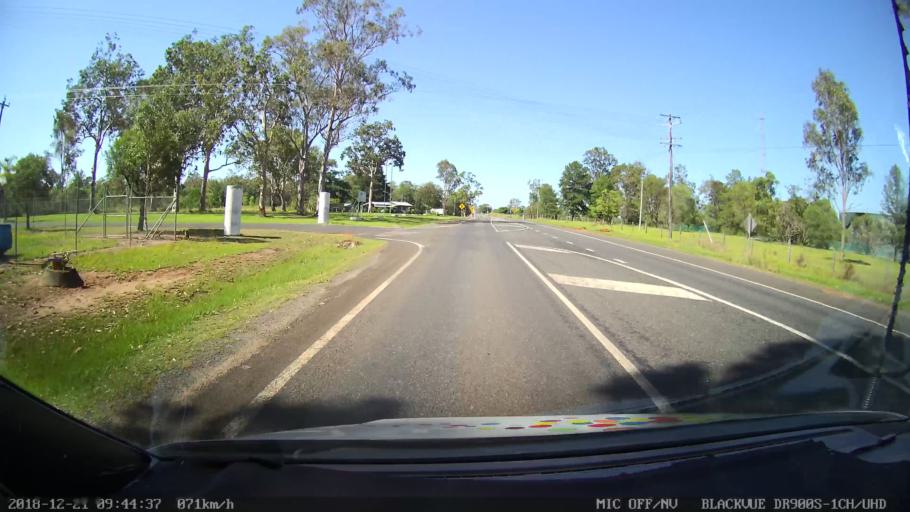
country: AU
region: New South Wales
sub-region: Clarence Valley
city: Grafton
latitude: -29.6200
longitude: 152.9325
